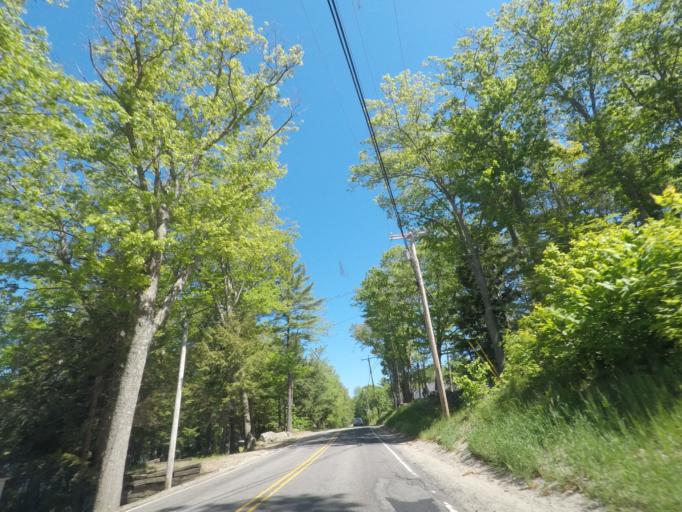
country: US
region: Maine
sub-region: Kennebec County
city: Manchester
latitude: 44.2814
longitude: -69.8894
